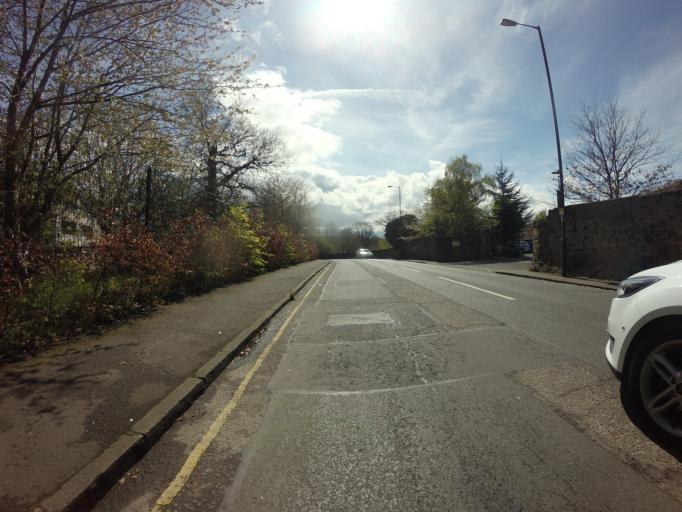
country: GB
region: Scotland
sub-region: West Lothian
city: Seafield
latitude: 55.9416
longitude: -3.1453
